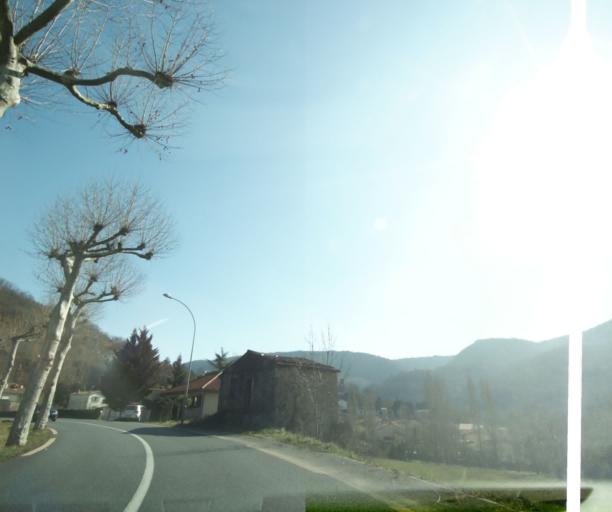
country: FR
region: Midi-Pyrenees
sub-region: Departement de l'Aveyron
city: Saint-Affrique
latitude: 43.9484
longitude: 2.9000
